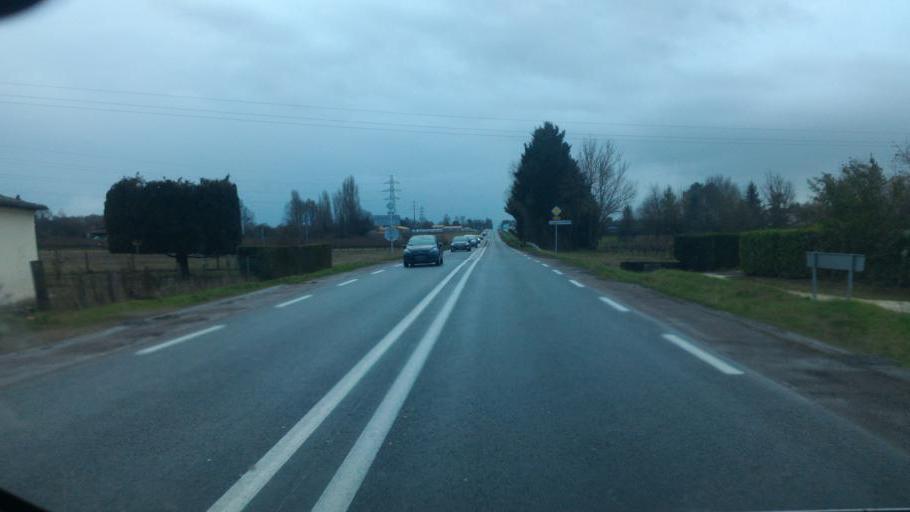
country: FR
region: Aquitaine
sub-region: Departement de la Gironde
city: Saint-Gervais
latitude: 45.0226
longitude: -0.4499
